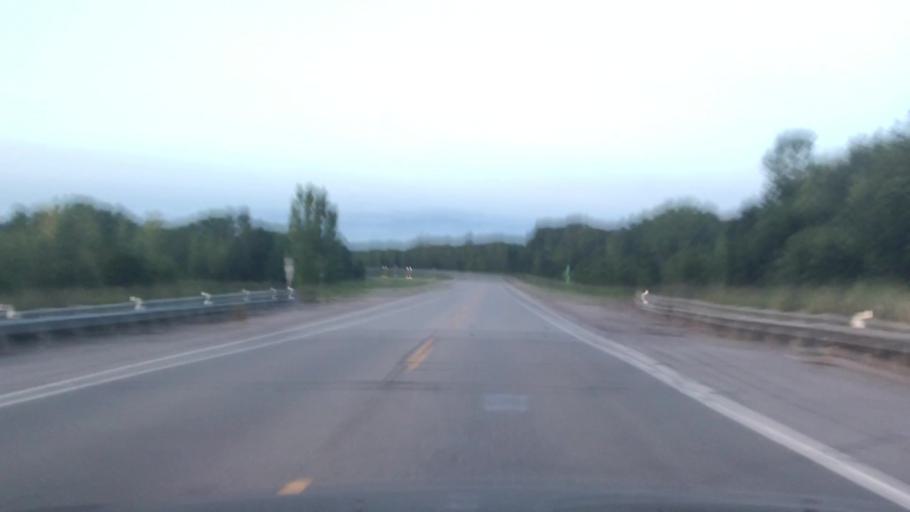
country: US
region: Minnesota
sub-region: Redwood County
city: Redwood Falls
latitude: 44.5415
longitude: -95.0018
